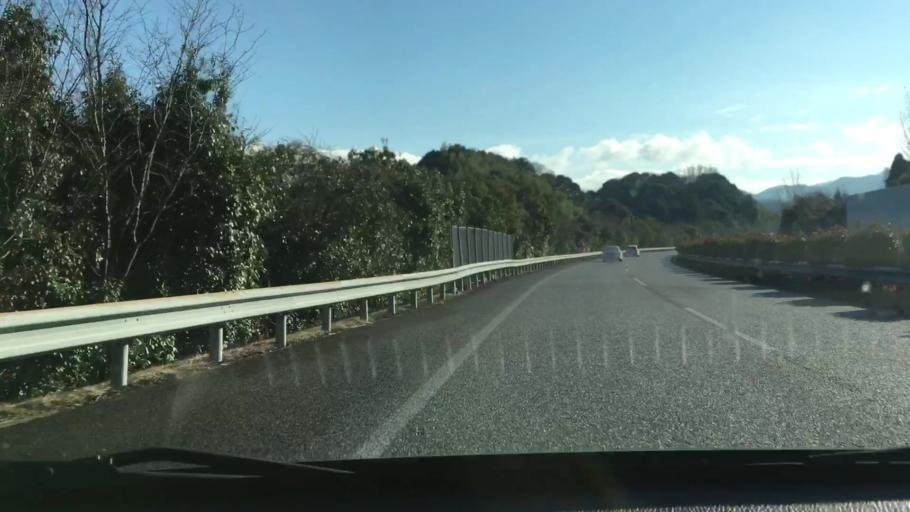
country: JP
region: Kumamoto
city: Hitoyoshi
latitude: 32.1955
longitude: 130.7779
